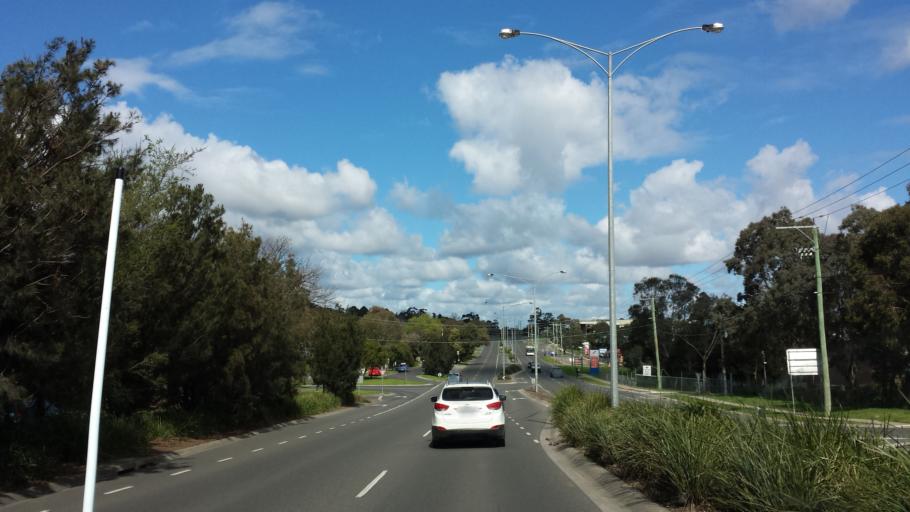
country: AU
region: Victoria
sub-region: Maroondah
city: Bayswater North
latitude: -37.8392
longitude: 145.2870
